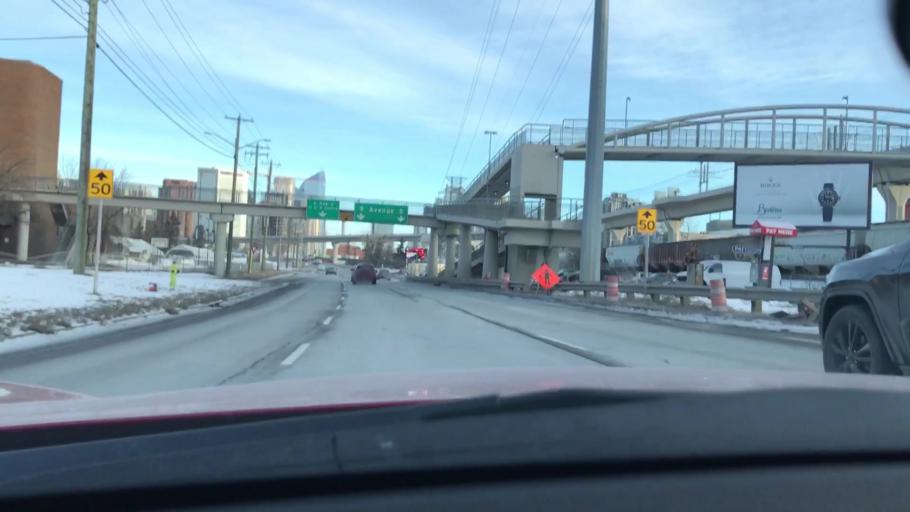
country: CA
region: Alberta
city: Calgary
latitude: 51.0454
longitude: -114.0996
